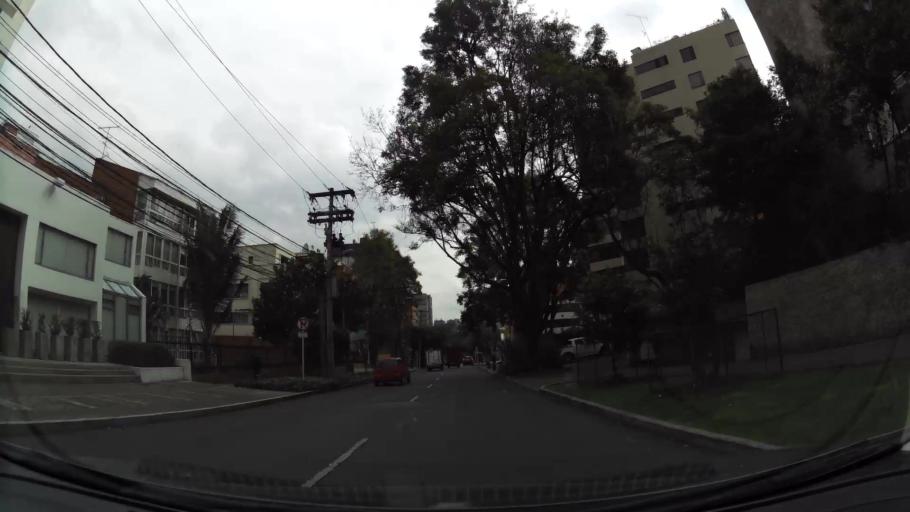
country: CO
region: Bogota D.C.
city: Barrio San Luis
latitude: 4.6616
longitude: -74.0532
